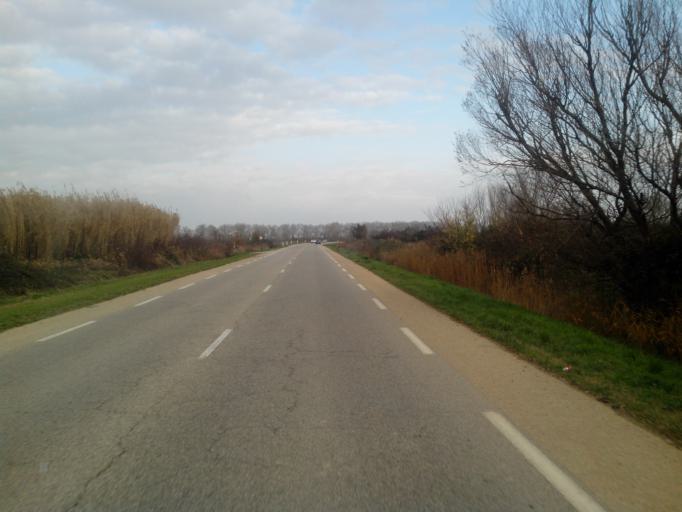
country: FR
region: Languedoc-Roussillon
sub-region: Departement du Gard
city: Saint-Gilles
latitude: 43.5792
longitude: 4.4349
